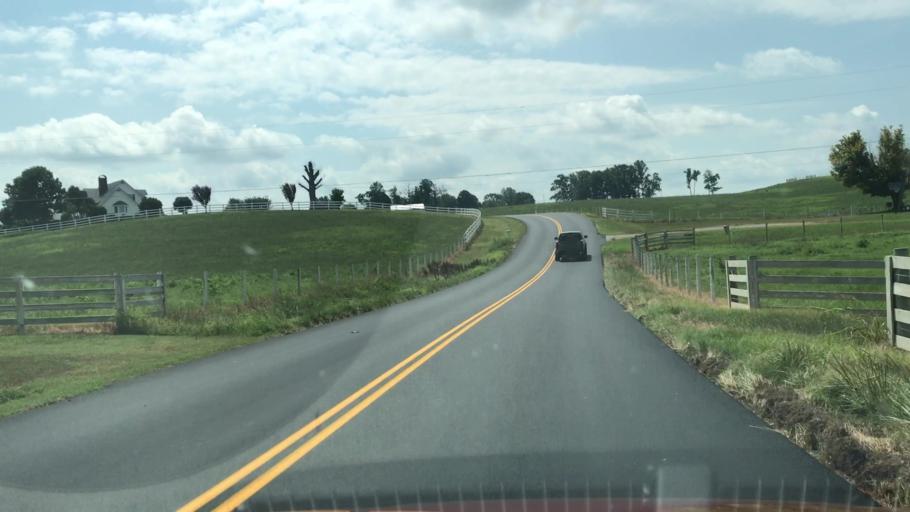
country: US
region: Kentucky
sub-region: Monroe County
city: Tompkinsville
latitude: 36.7308
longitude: -85.7294
